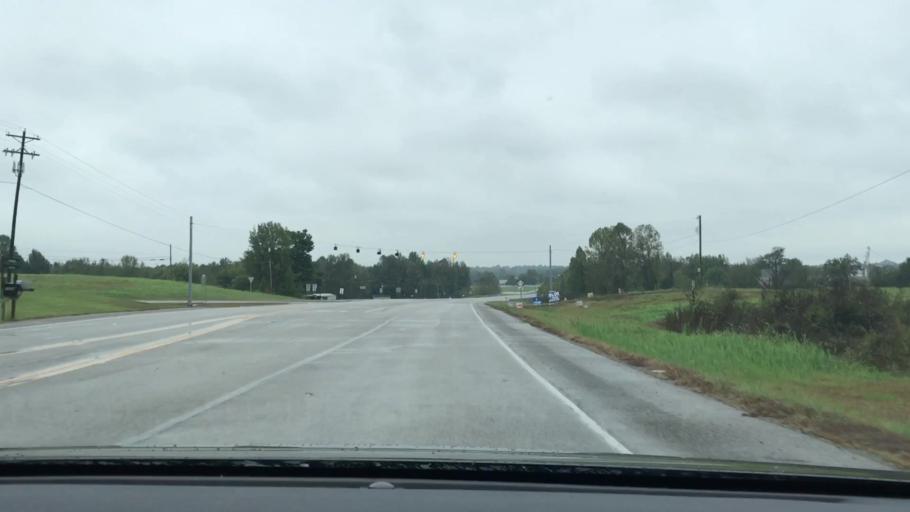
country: US
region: Kentucky
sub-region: Hopkins County
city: Madisonville
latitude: 37.3359
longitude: -87.4167
